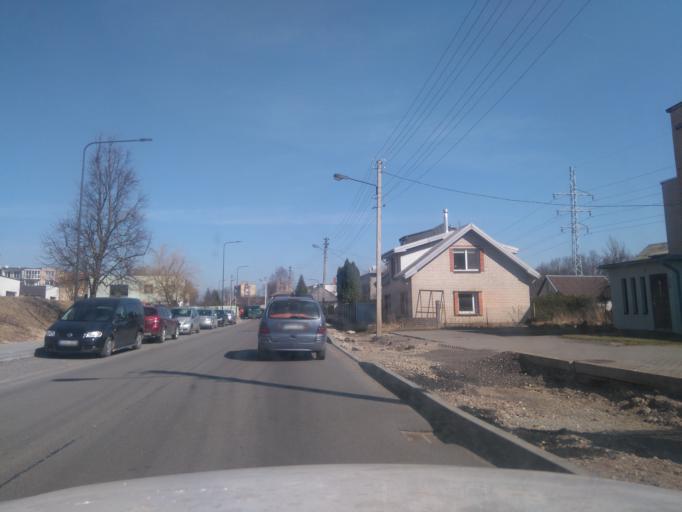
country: LT
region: Kauno apskritis
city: Dainava (Kaunas)
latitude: 54.8875
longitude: 23.9541
